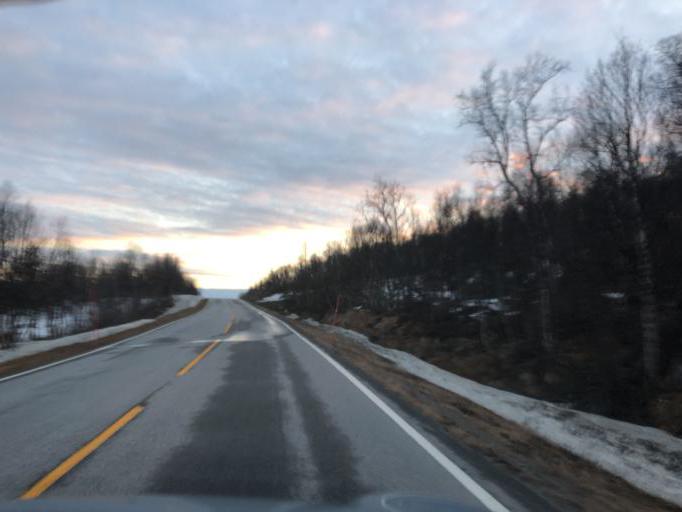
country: NO
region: Sor-Trondelag
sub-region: Tydal
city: Aas
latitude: 62.6364
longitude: 11.9464
